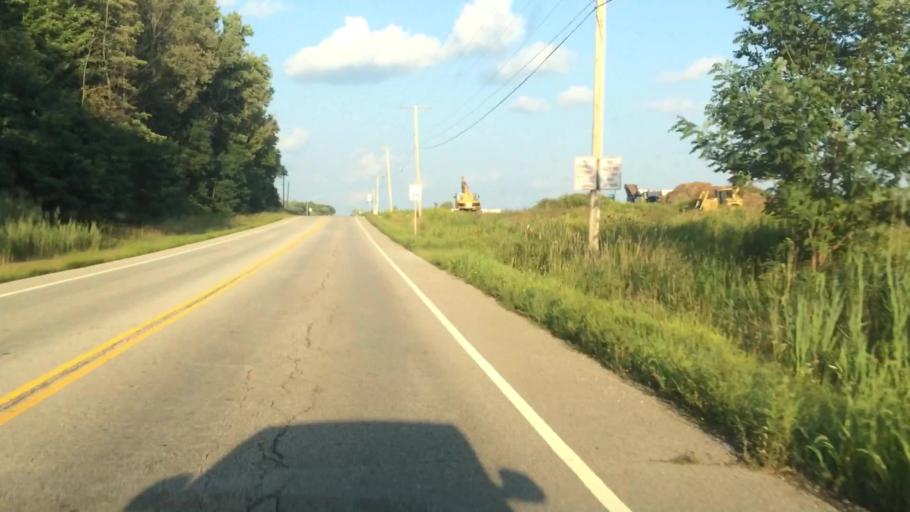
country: US
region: Ohio
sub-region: Summit County
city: Silver Lake
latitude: 41.2031
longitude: -81.4919
